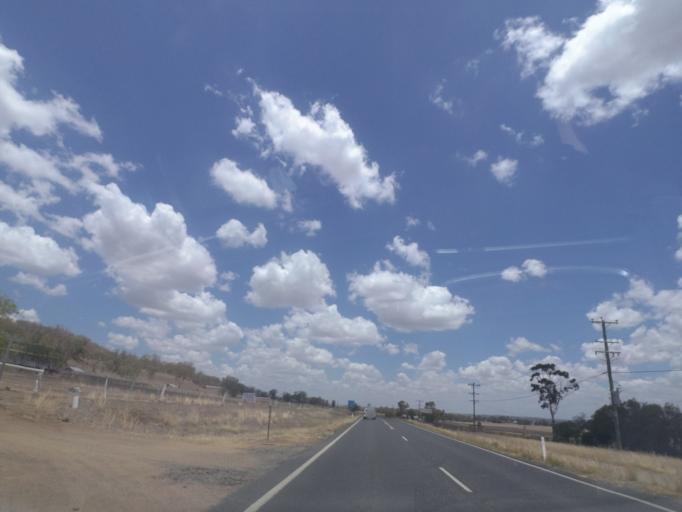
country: AU
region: Queensland
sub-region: Southern Downs
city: Warwick
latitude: -28.0191
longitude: 151.9858
